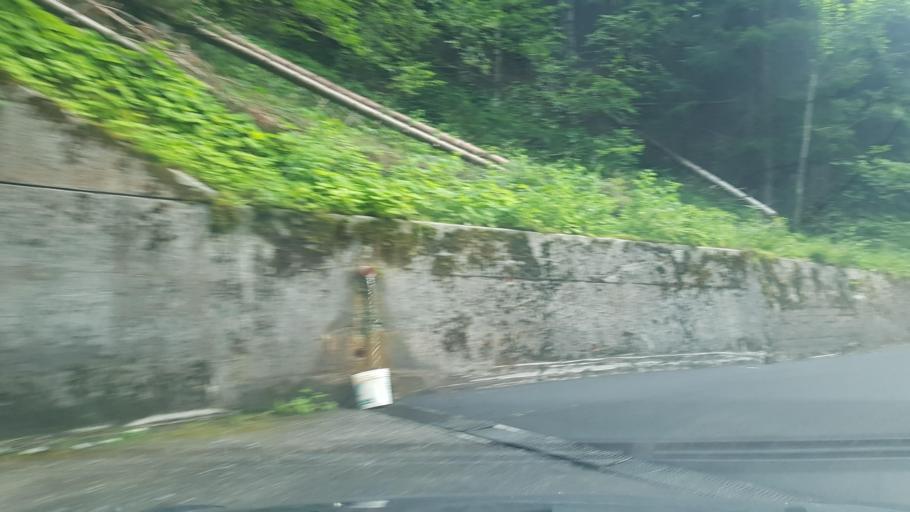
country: IT
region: Friuli Venezia Giulia
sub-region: Provincia di Udine
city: Paularo
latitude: 46.5556
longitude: 13.1288
